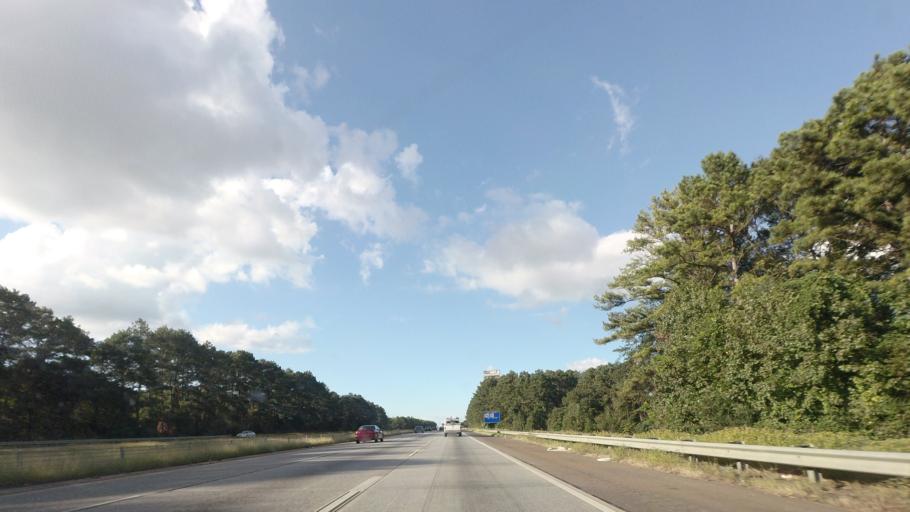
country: US
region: Georgia
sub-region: Houston County
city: Centerville
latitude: 32.5690
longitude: -83.7437
